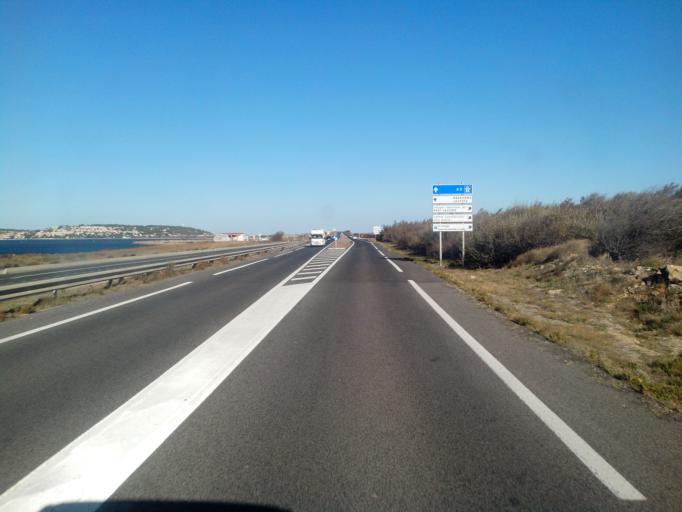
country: FR
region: Languedoc-Roussillon
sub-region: Departement de l'Aude
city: Leucate
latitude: 42.8803
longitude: 3.0429
